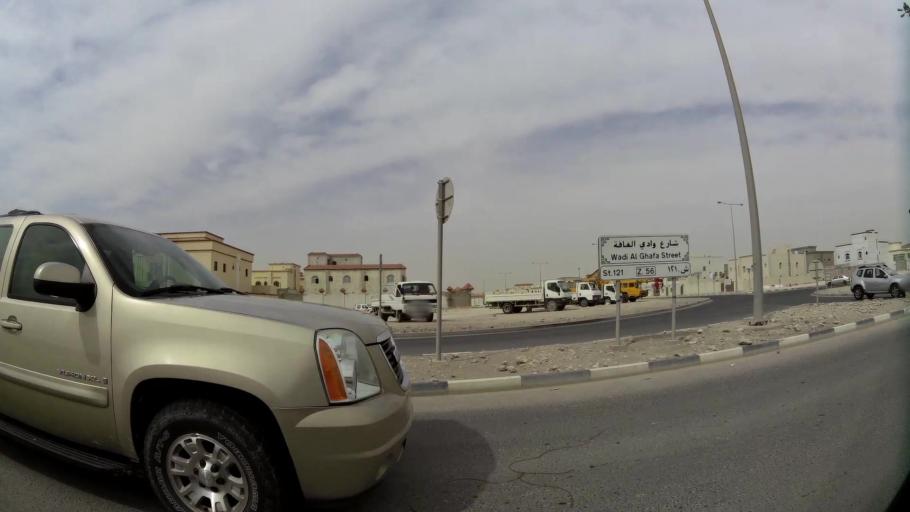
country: QA
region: Baladiyat ad Dawhah
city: Doha
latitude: 25.2122
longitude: 51.4821
